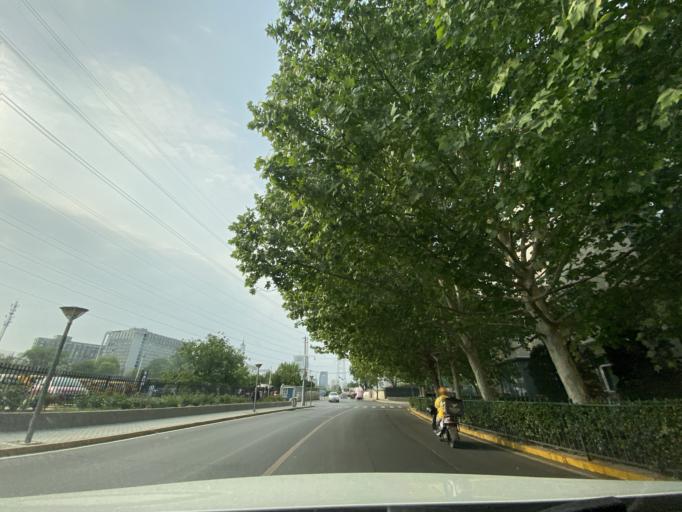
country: CN
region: Beijing
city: Haidian
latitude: 39.9766
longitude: 116.3356
